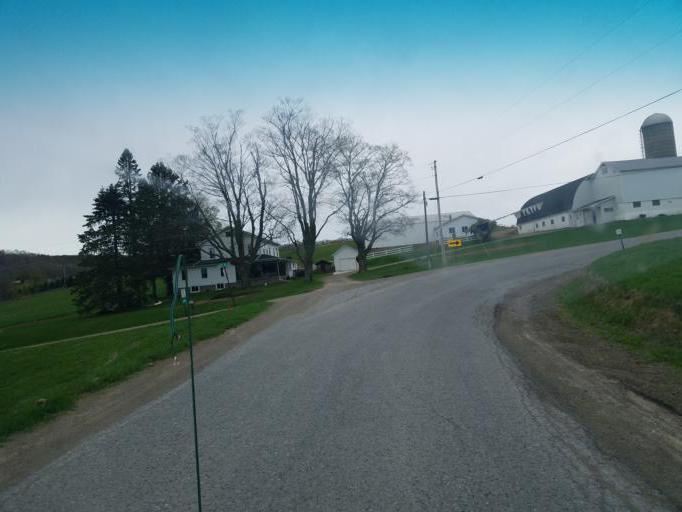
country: US
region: Pennsylvania
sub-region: Potter County
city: Galeton
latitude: 41.8875
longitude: -77.7380
